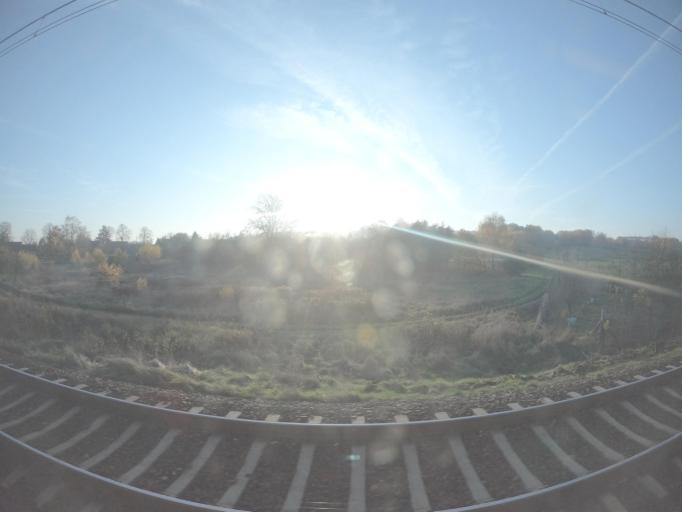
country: PL
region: Lubusz
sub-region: Powiat sulecinski
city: Torzym
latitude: 52.2566
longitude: 14.9496
